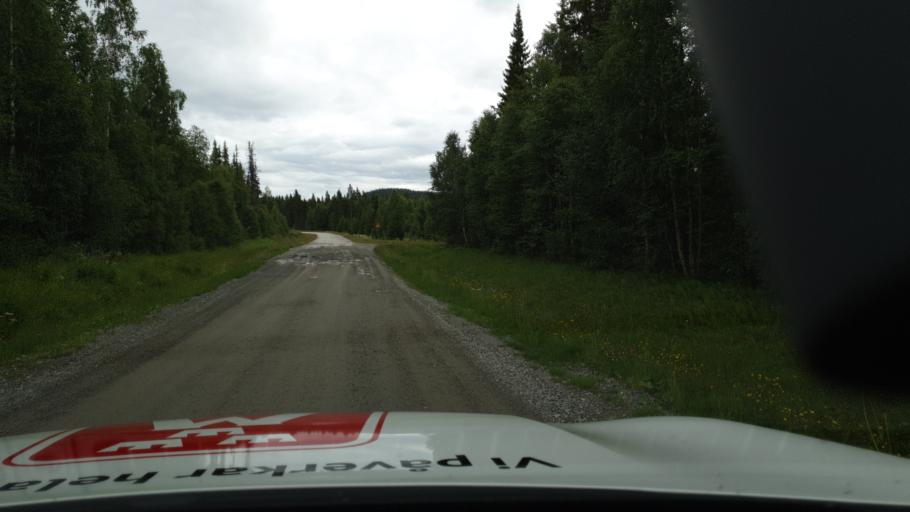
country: SE
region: Vaesterbotten
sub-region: Storumans Kommun
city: Storuman
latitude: 64.7114
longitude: 17.0945
